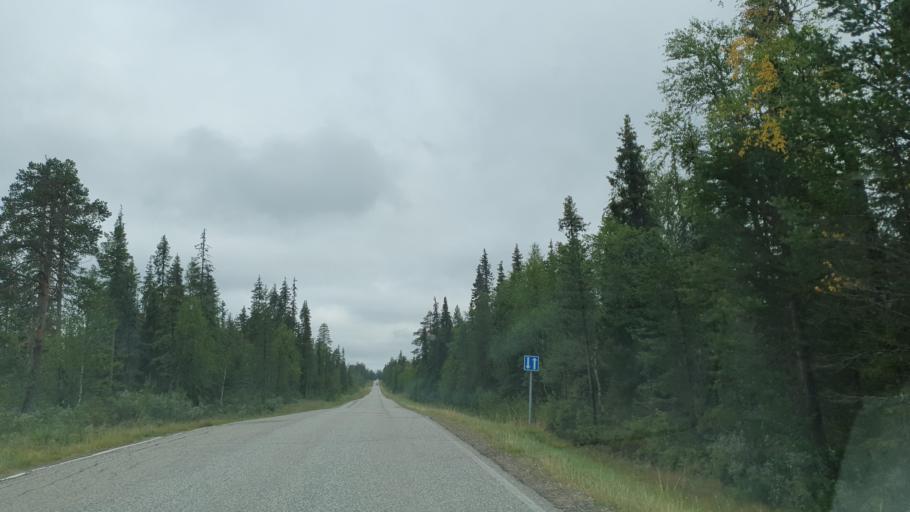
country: FI
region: Lapland
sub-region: Tunturi-Lappi
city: Muonio
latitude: 67.8024
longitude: 24.0776
